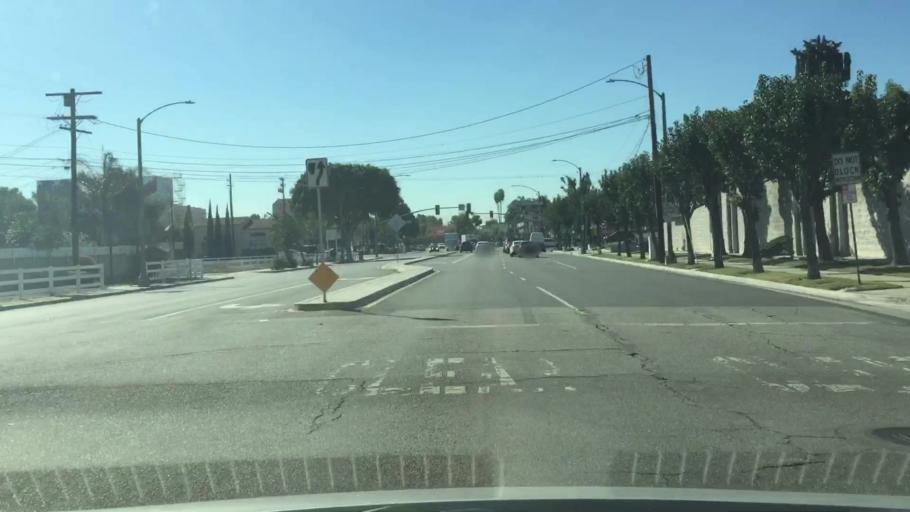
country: US
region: California
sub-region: Los Angeles County
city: East Rancho Dominguez
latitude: 33.8758
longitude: -118.1861
